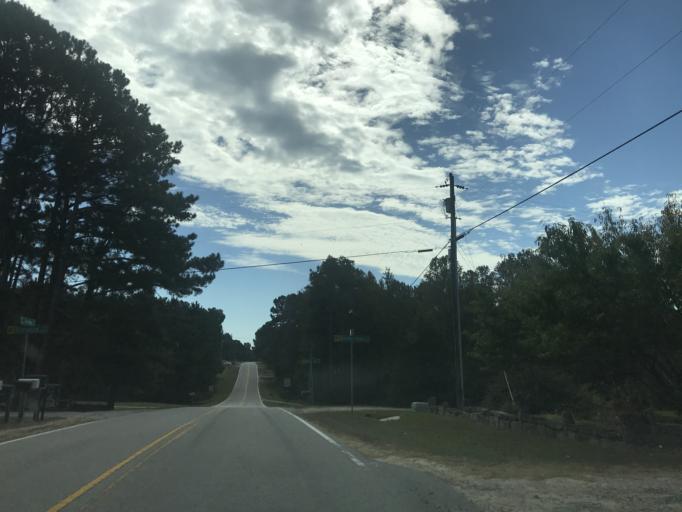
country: US
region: North Carolina
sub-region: Wake County
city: Rolesville
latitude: 35.8706
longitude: -78.4773
